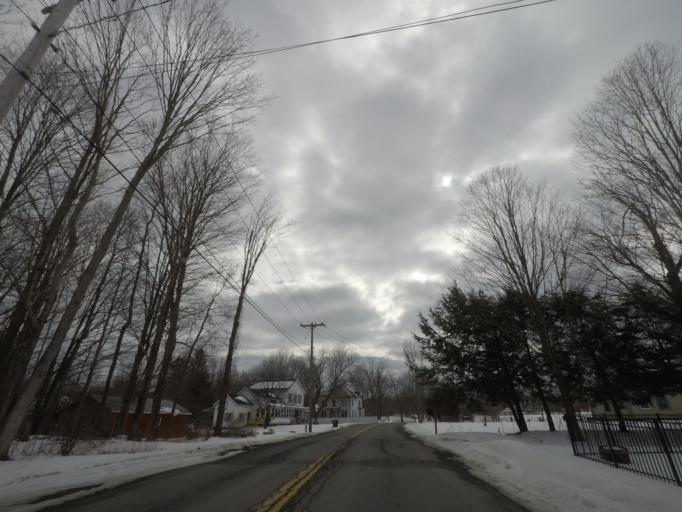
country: US
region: New York
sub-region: Washington County
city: Cambridge
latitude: 42.9526
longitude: -73.4333
